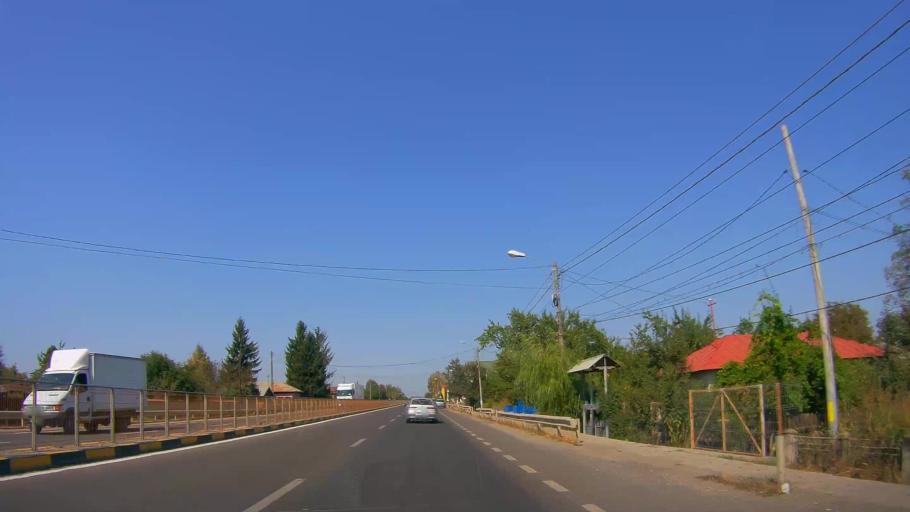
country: RO
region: Giurgiu
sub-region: Comuna Fratesti
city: Remus
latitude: 43.9399
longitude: 25.9782
